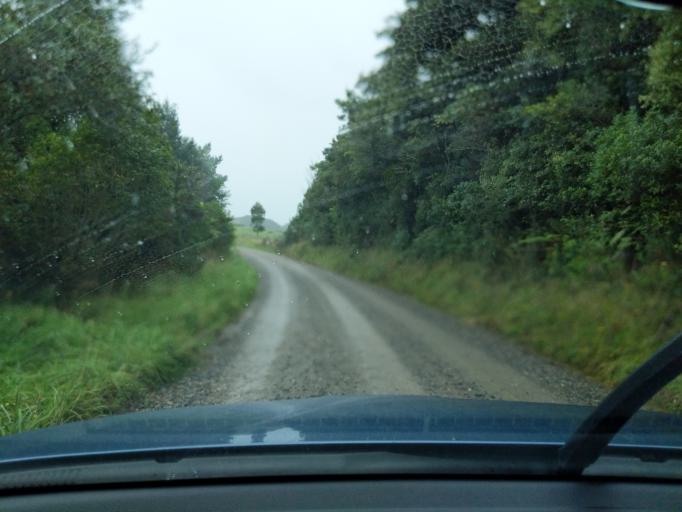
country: NZ
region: Tasman
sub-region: Tasman District
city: Takaka
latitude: -40.6307
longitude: 172.4911
